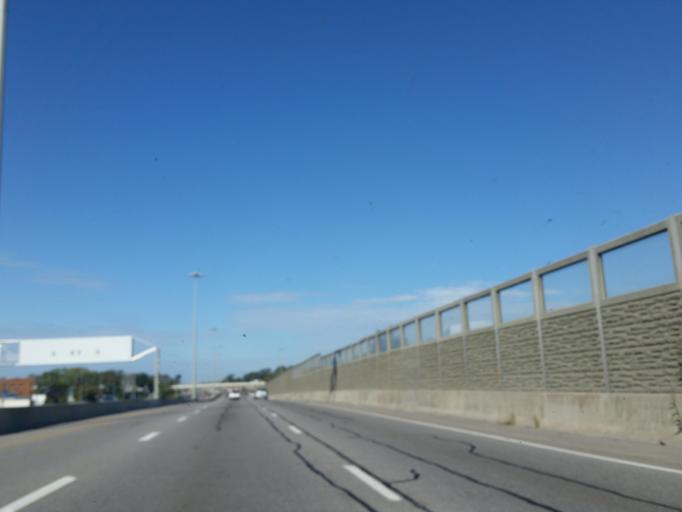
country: CA
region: Ontario
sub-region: Regional Municipality of Niagara
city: St. Catharines
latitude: 43.1718
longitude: -79.2246
